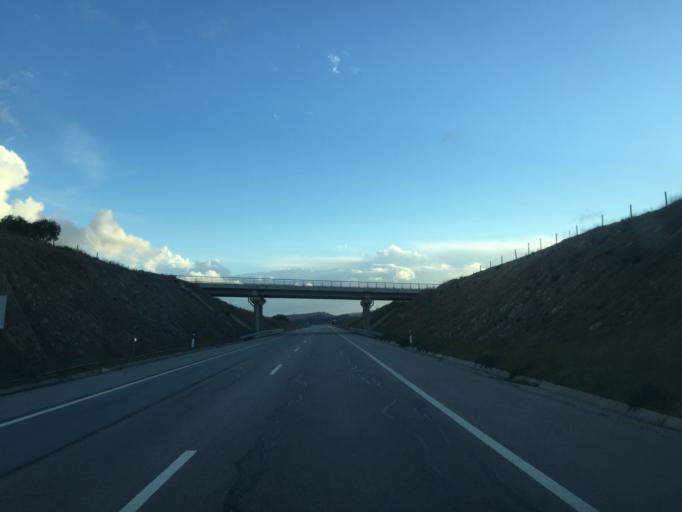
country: PT
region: Guarda
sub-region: Meda
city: Meda
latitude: 40.9242
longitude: -7.2038
